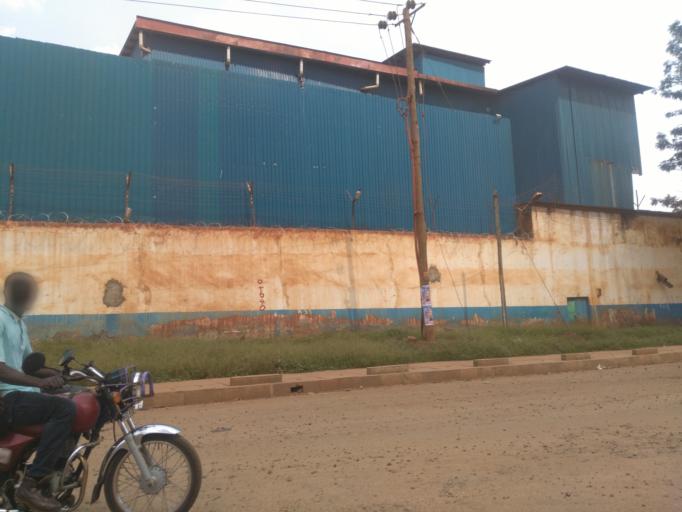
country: UG
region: Eastern Region
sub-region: Jinja District
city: Jinja
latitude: 0.4357
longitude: 33.2132
